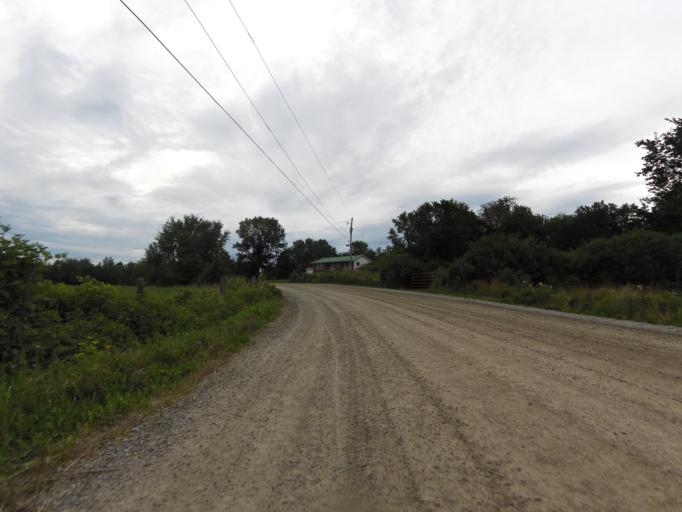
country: CA
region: Ontario
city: Carleton Place
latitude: 45.1578
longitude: -76.1897
